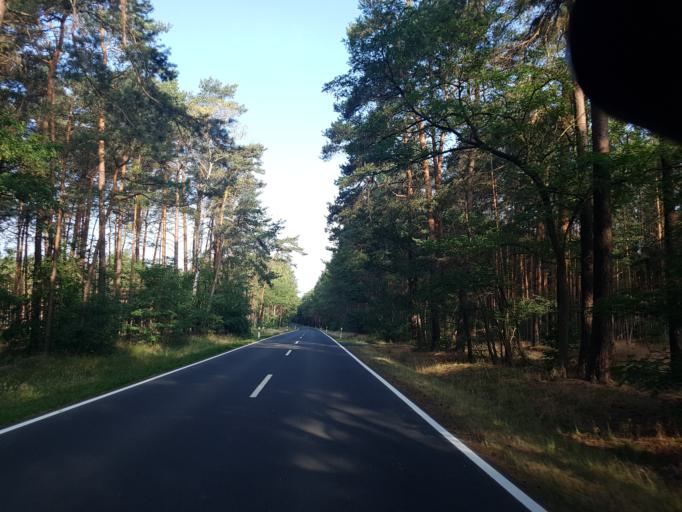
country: DE
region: Saxony-Anhalt
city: Holzdorf
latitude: 51.8491
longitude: 13.1352
